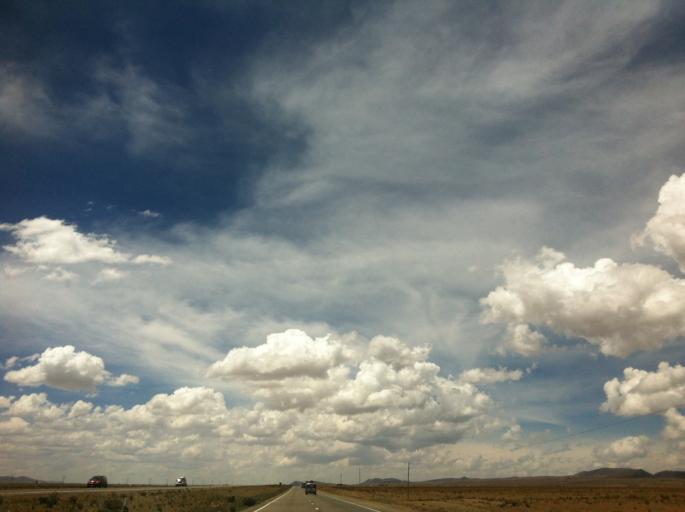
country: BO
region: La Paz
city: Patacamaya
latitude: -17.0773
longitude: -68.0192
